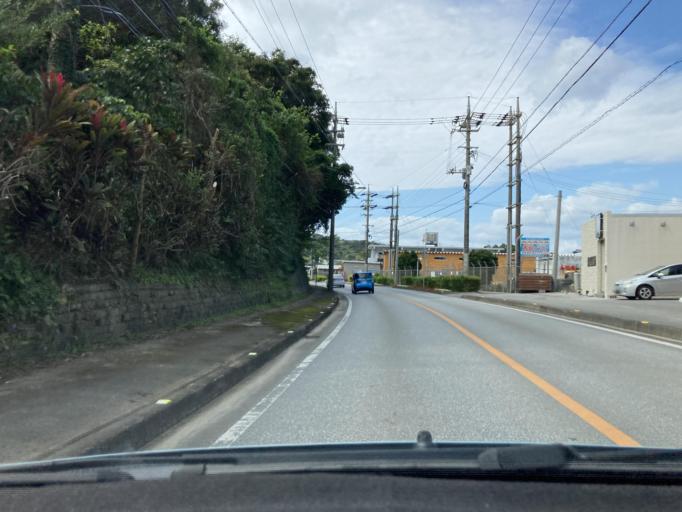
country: JP
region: Okinawa
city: Nago
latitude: 26.6569
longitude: 127.9073
